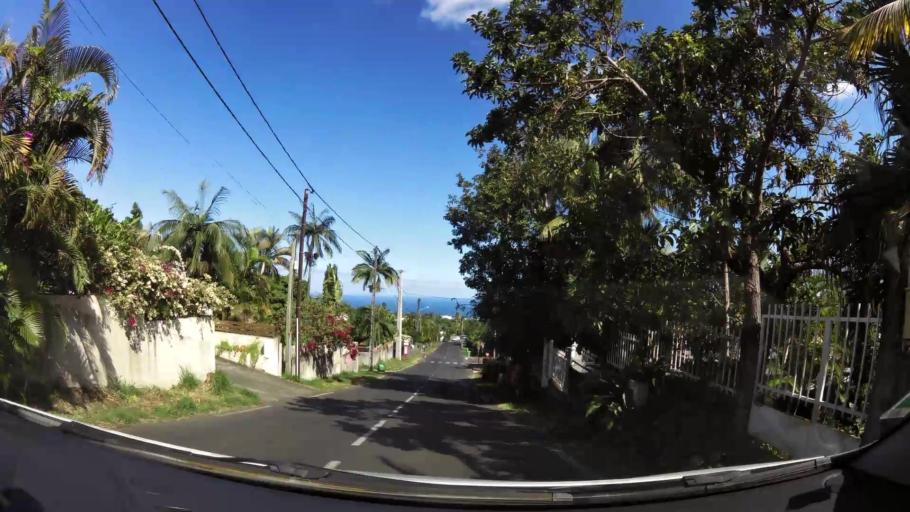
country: RE
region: Reunion
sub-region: Reunion
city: Le Tampon
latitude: -21.2891
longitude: 55.5082
